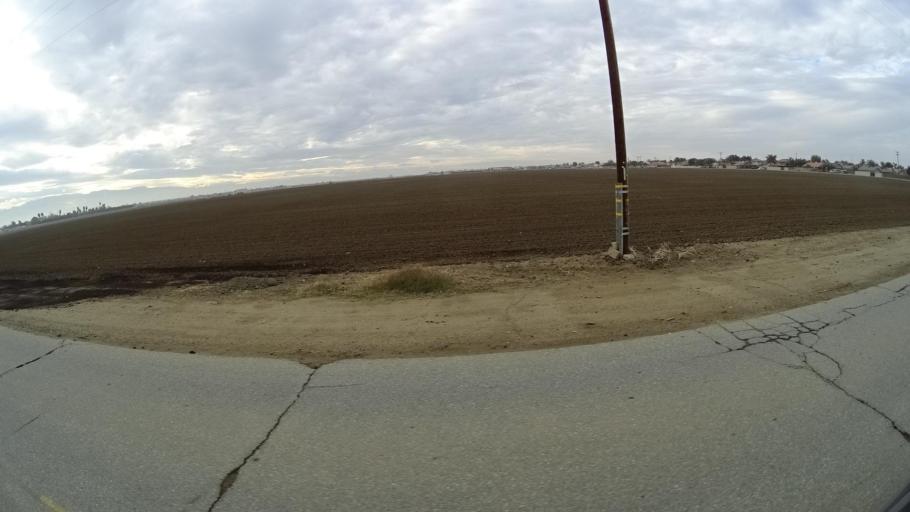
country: US
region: California
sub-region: Kern County
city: Arvin
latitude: 35.1854
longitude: -118.8240
